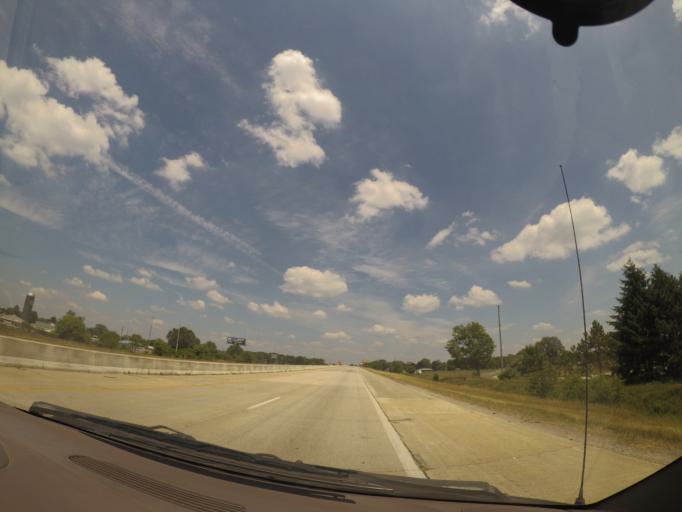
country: US
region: Indiana
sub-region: Elkhart County
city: Dunlap
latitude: 41.6449
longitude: -85.9563
